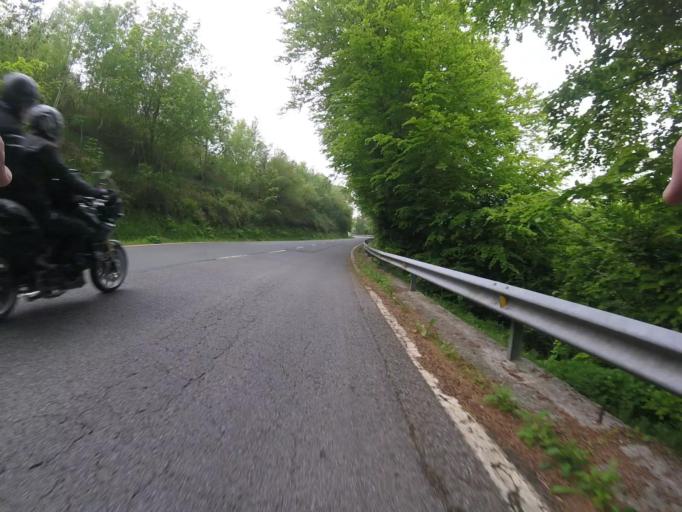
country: ES
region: Navarre
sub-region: Provincia de Navarra
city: Zugarramurdi
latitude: 43.2523
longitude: -1.4832
